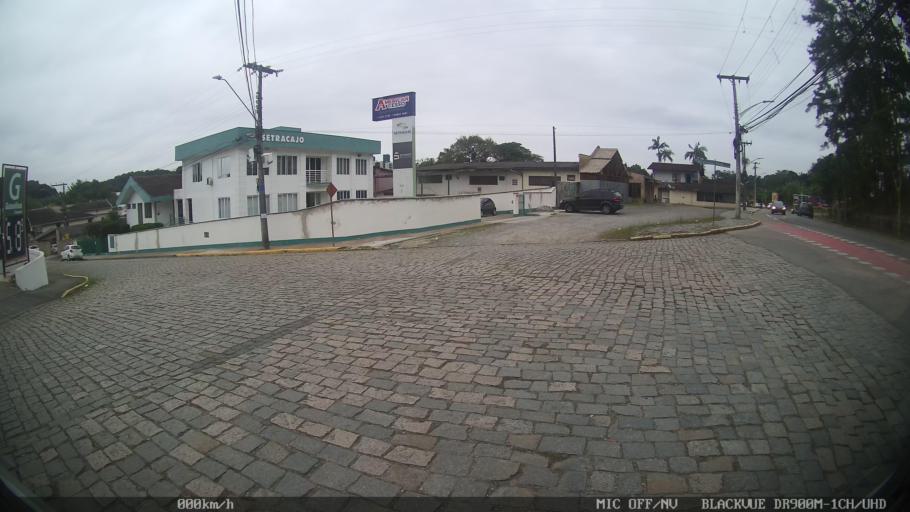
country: BR
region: Santa Catarina
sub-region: Joinville
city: Joinville
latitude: -26.3134
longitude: -48.8588
